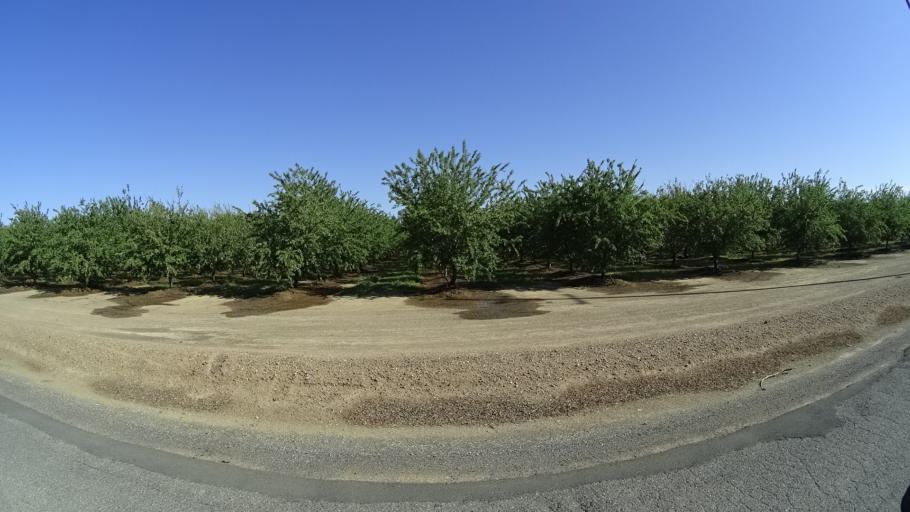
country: US
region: California
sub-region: Glenn County
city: Orland
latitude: 39.7542
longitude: -122.1612
